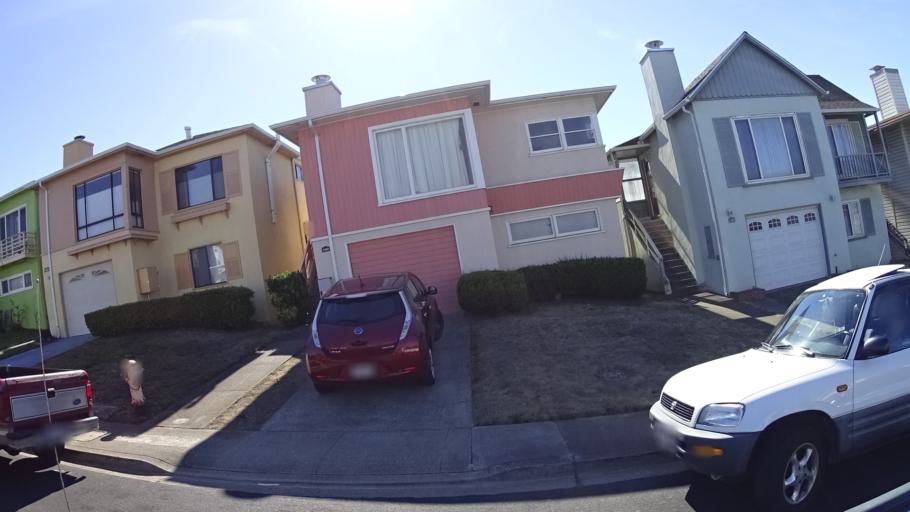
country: US
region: California
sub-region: San Mateo County
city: Broadmoor
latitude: 37.6895
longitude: -122.4905
